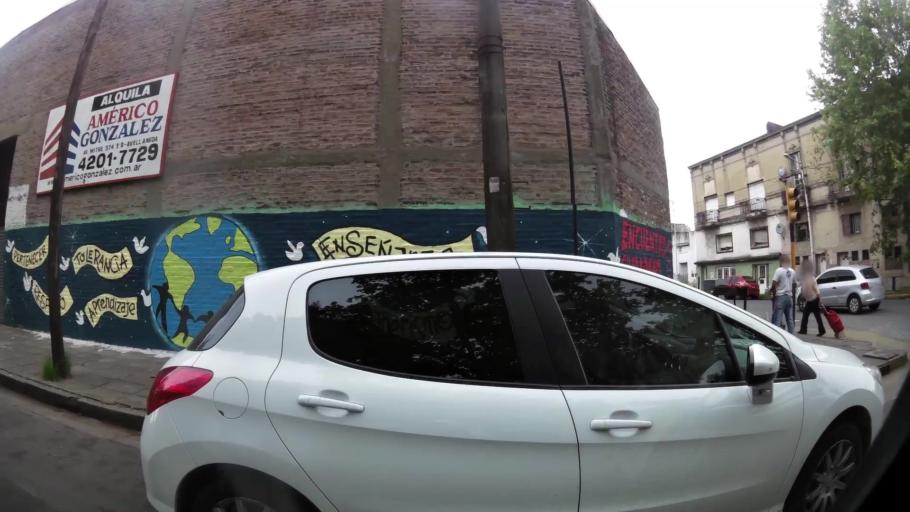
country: AR
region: Buenos Aires
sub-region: Partido de Avellaneda
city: Avellaneda
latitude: -34.6591
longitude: -58.3630
